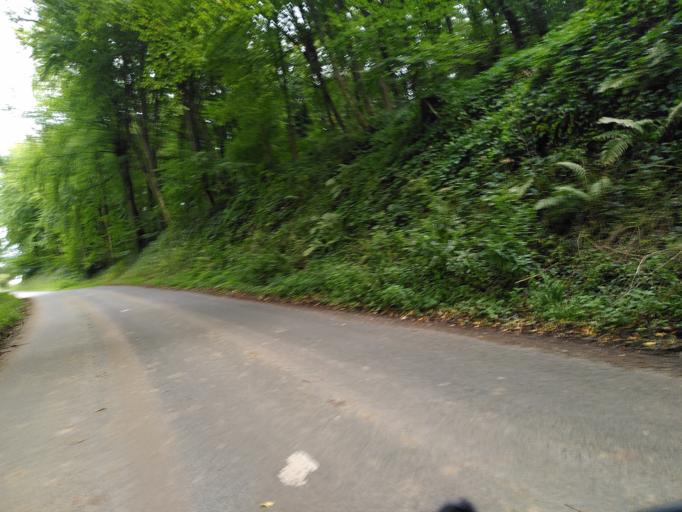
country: FR
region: Nord-Pas-de-Calais
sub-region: Departement du Pas-de-Calais
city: Desvres
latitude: 50.6638
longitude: 1.8695
